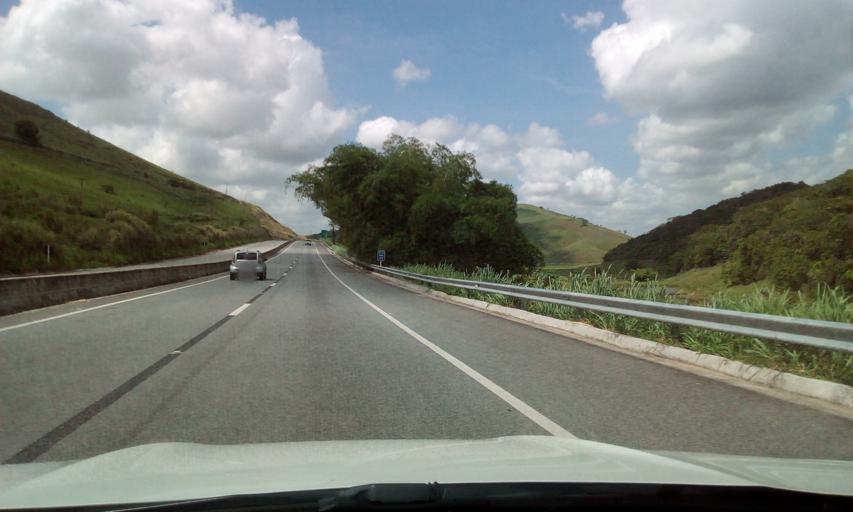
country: BR
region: Alagoas
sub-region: Flexeiras
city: Flexeiras
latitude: -9.2494
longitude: -35.7672
